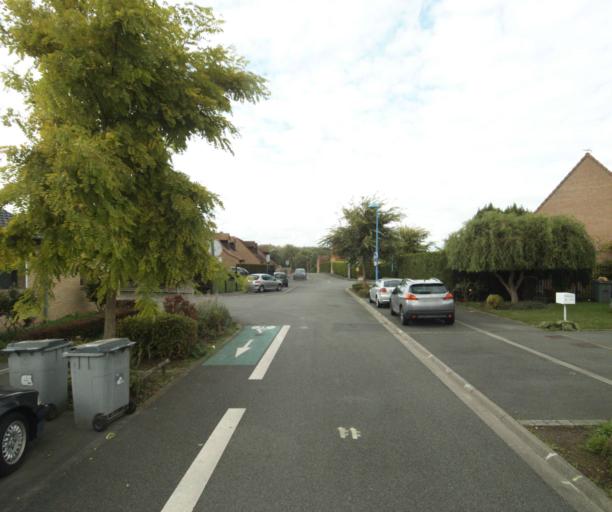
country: FR
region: Nord-Pas-de-Calais
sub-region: Departement du Nord
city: Perenchies
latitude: 50.6635
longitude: 2.9609
